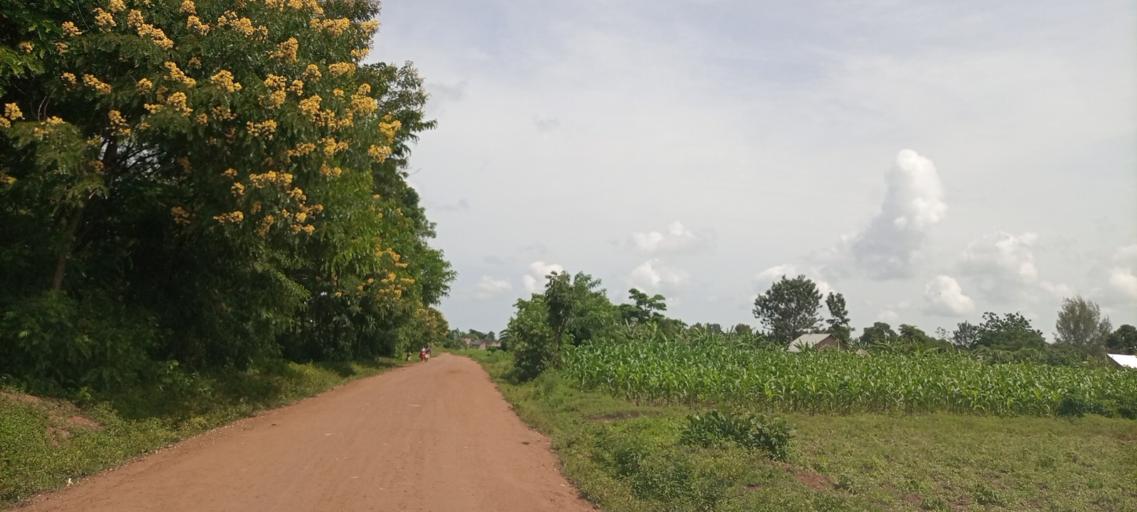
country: UG
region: Eastern Region
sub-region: Budaka District
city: Budaka
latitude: 1.1708
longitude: 33.9369
